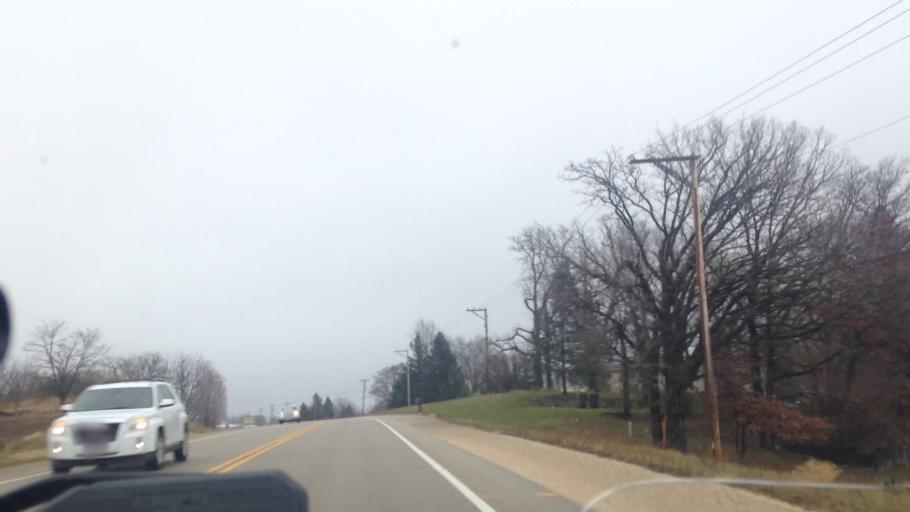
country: US
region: Wisconsin
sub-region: Dodge County
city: Beaver Dam
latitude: 43.4450
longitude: -88.7754
